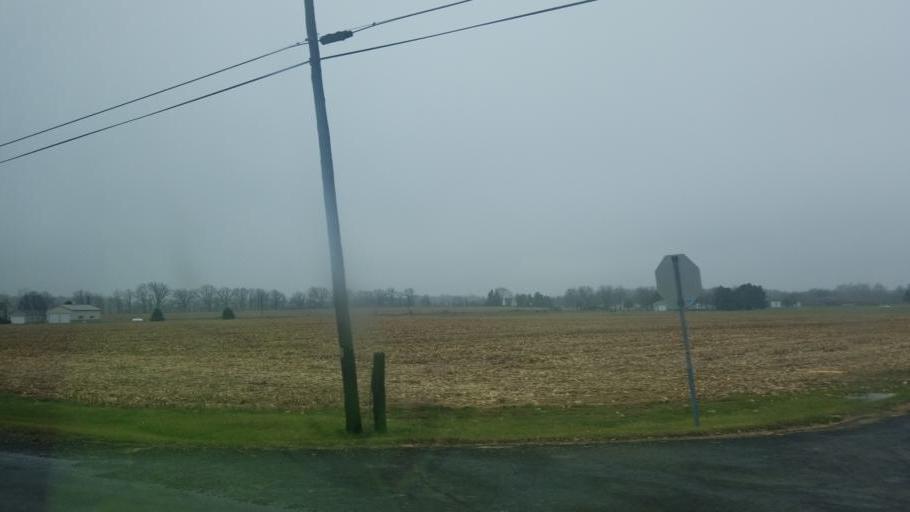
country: US
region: Ohio
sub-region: Union County
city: New California
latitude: 40.1833
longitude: -83.2781
